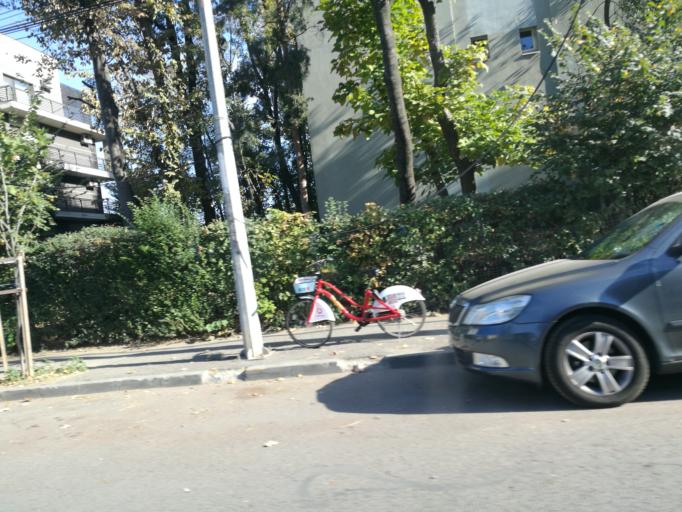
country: RO
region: Ilfov
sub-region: Comuna Chiajna
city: Rosu
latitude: 44.4376
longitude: 26.0144
